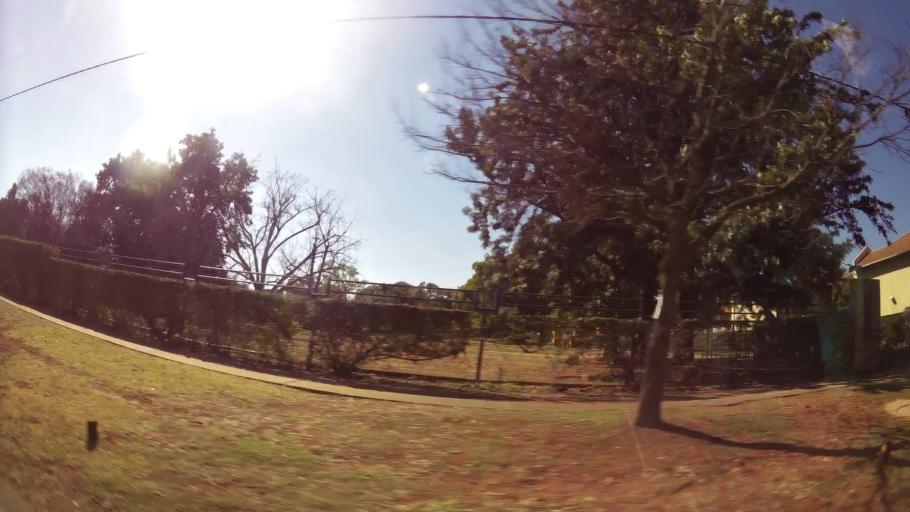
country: ZA
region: Gauteng
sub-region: City of Tshwane Metropolitan Municipality
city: Centurion
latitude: -25.8440
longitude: 28.1905
